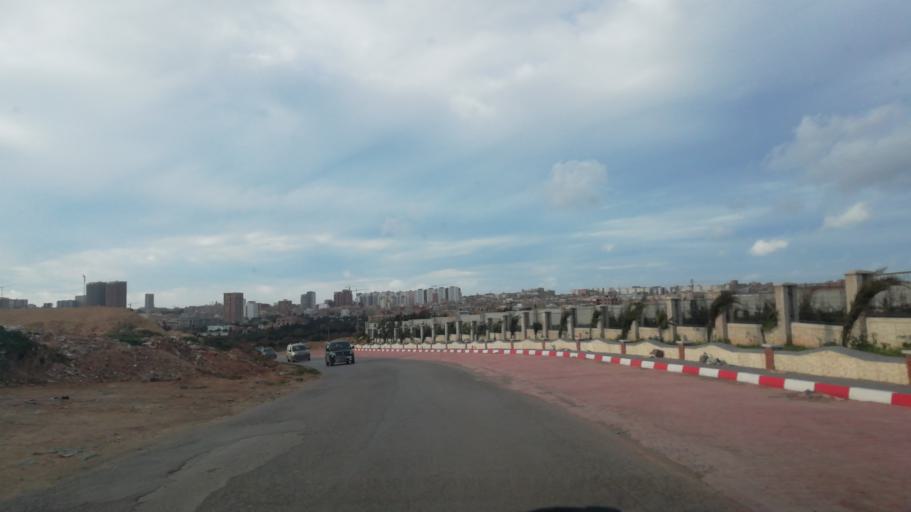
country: DZ
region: Oran
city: Bir el Djir
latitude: 35.7159
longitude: -0.5583
